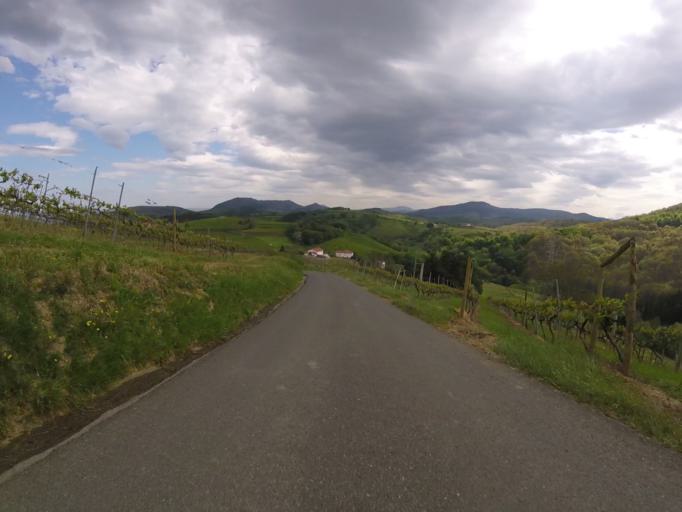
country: ES
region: Basque Country
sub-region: Provincia de Guipuzcoa
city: Zarautz
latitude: 43.2585
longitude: -2.1724
